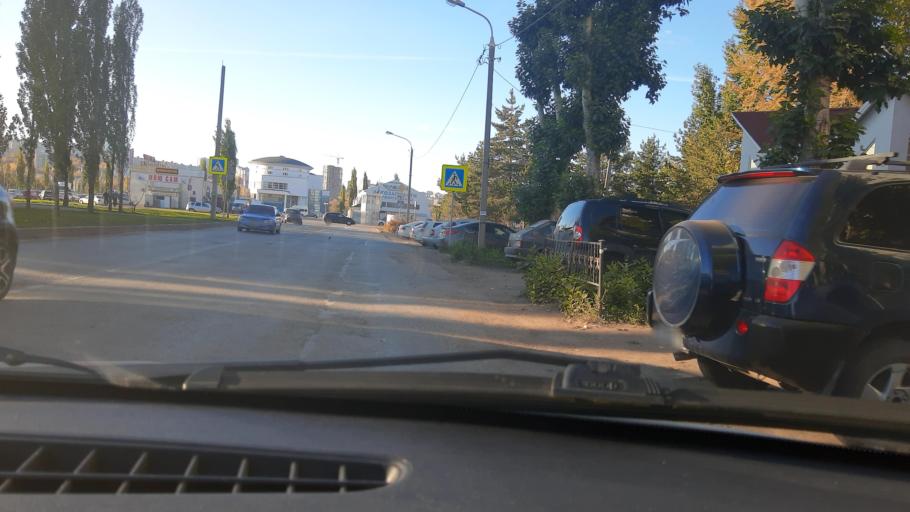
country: RU
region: Bashkortostan
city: Ufa
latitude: 54.7715
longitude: 56.0660
